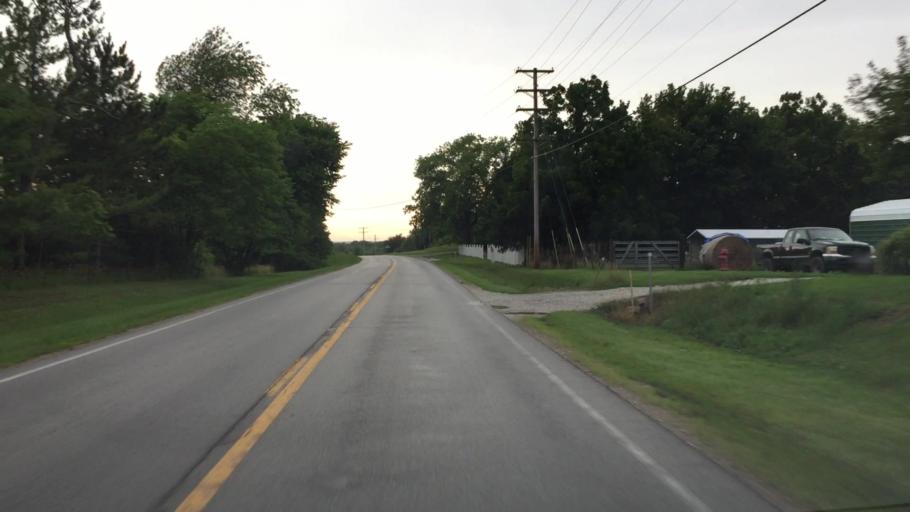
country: US
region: Illinois
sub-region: Hancock County
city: Warsaw
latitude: 40.3551
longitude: -91.4078
